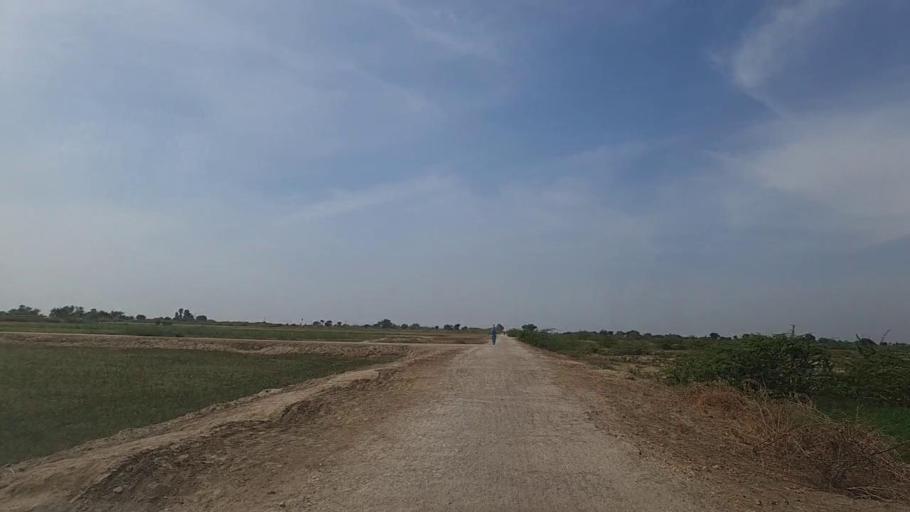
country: PK
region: Sindh
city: Kunri
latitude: 25.2127
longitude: 69.4936
